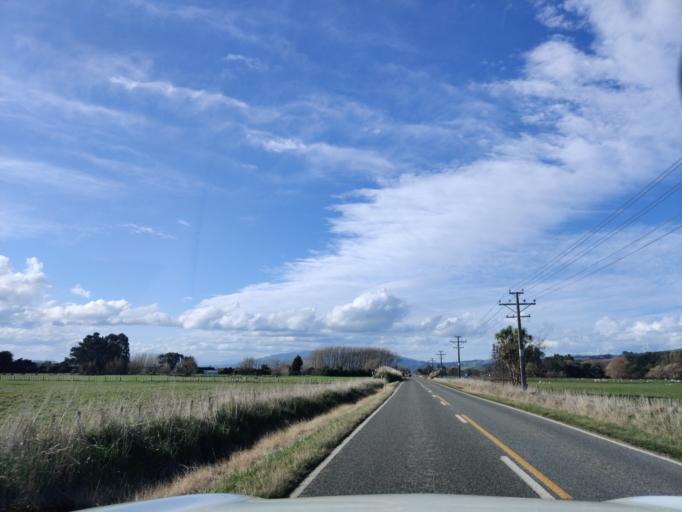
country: NZ
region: Manawatu-Wanganui
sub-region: Palmerston North City
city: Palmerston North
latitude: -40.3561
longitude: 175.6872
